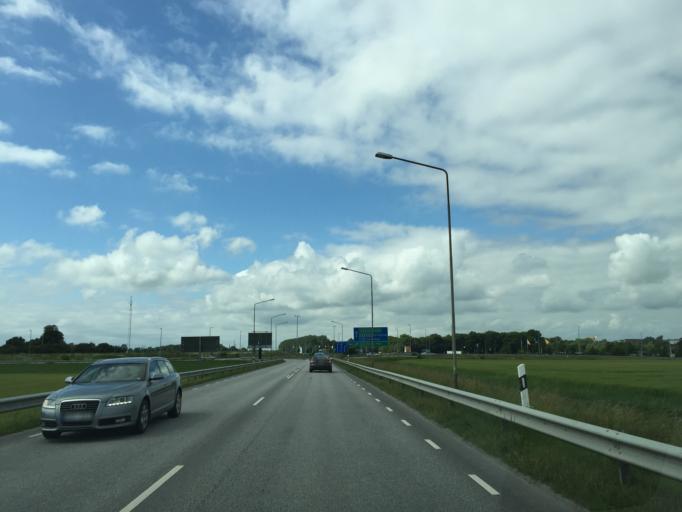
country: SE
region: Skane
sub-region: Lunds Kommun
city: Lund
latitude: 55.6766
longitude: 13.1842
